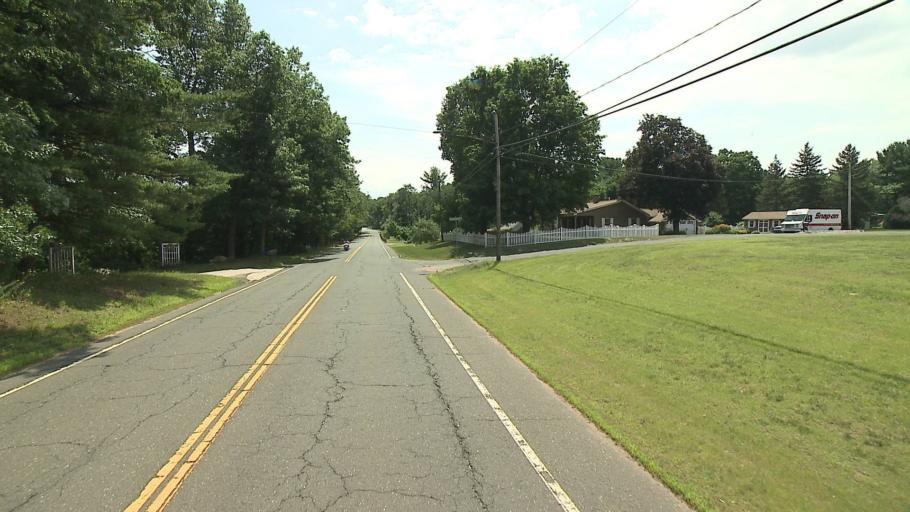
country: US
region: Massachusetts
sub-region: Hampden County
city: Southwick
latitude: 42.0246
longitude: -72.7487
